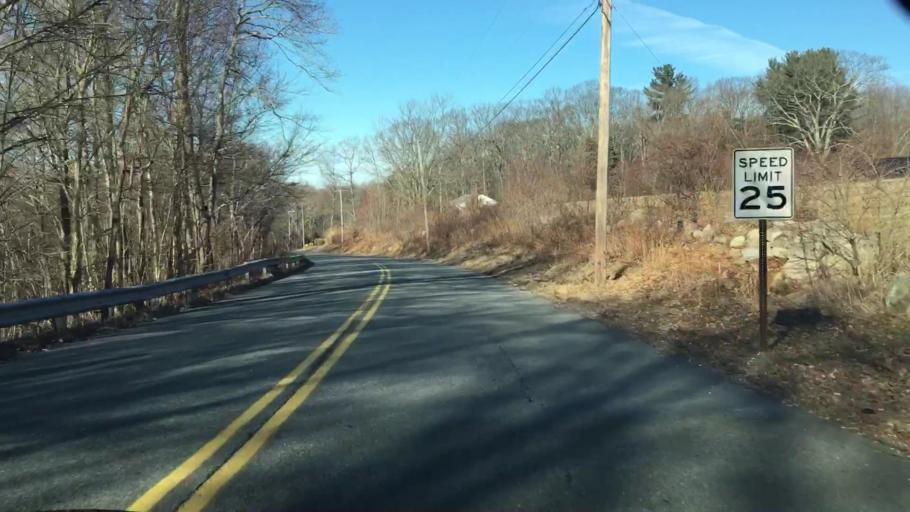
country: US
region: Connecticut
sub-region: Tolland County
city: Tolland
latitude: 41.8896
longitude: -72.3866
